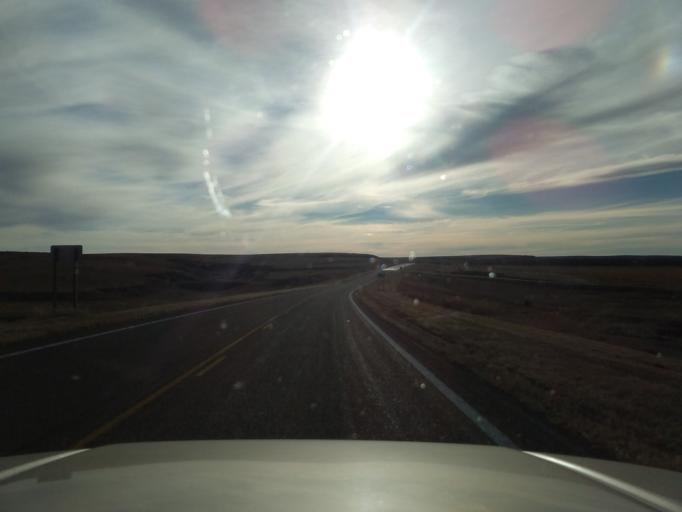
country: US
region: Kansas
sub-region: Norton County
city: Norton
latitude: 39.7327
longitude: -100.1776
